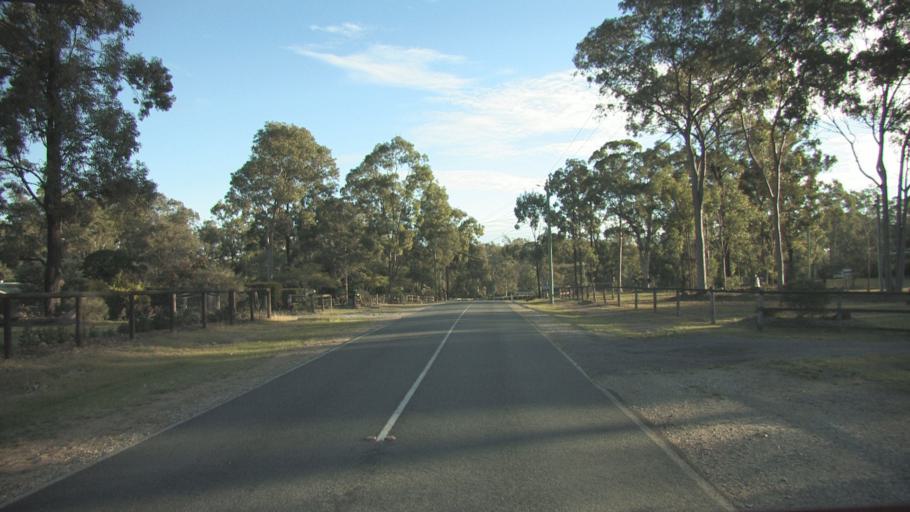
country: AU
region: Queensland
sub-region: Logan
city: Waterford West
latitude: -27.7323
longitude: 153.1411
